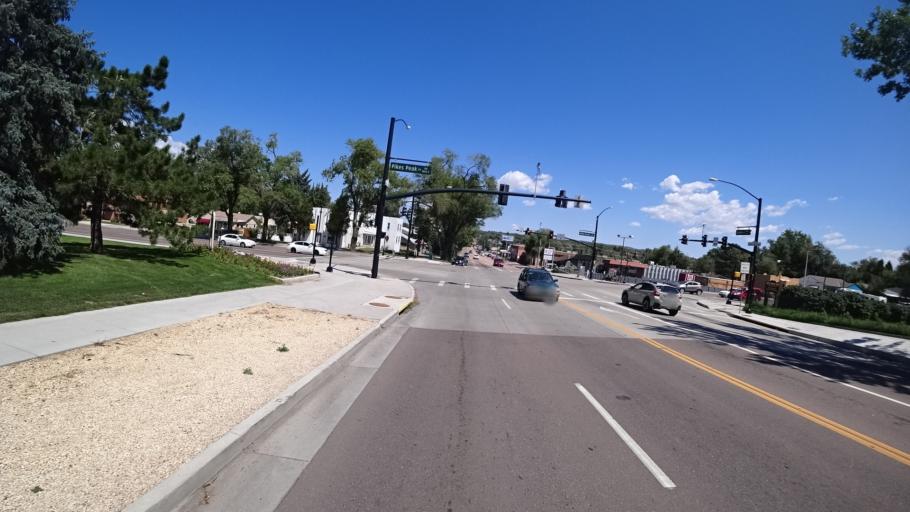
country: US
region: Colorado
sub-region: El Paso County
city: Colorado Springs
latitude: 38.8326
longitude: -104.7948
